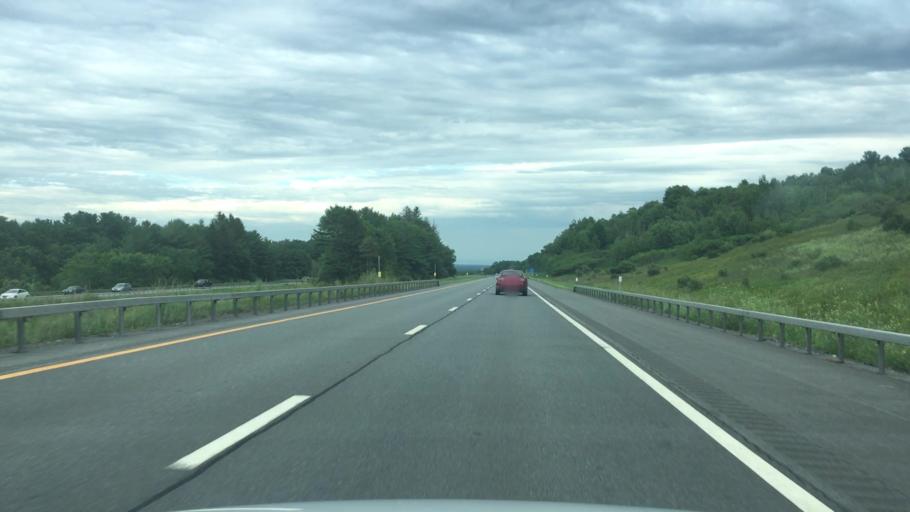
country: US
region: New York
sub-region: Albany County
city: Altamont
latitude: 42.7714
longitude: -74.0791
